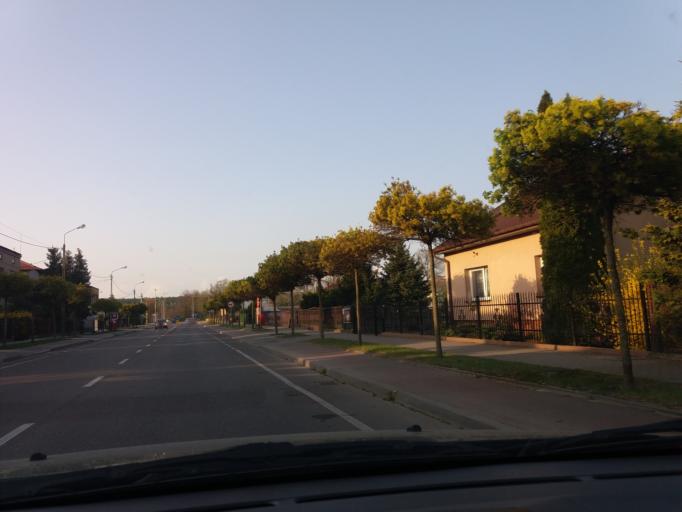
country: PL
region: Masovian Voivodeship
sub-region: Powiat mlawski
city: Mlawa
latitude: 53.1218
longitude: 20.3775
